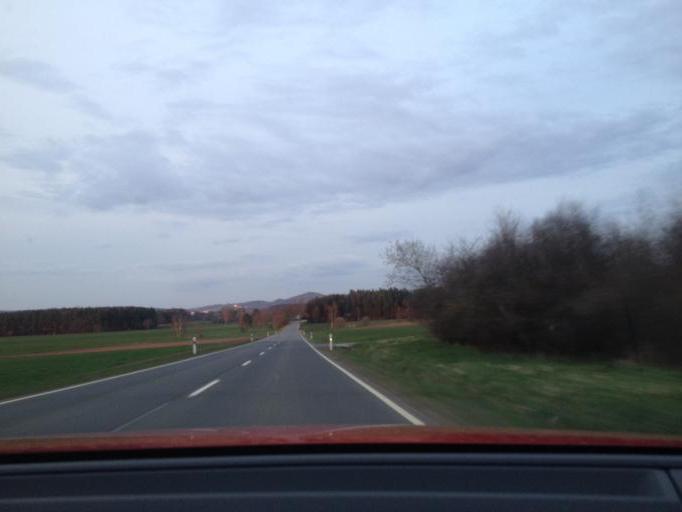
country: DE
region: Bavaria
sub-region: Upper Palatinate
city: Kastl
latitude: 49.8383
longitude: 11.8456
